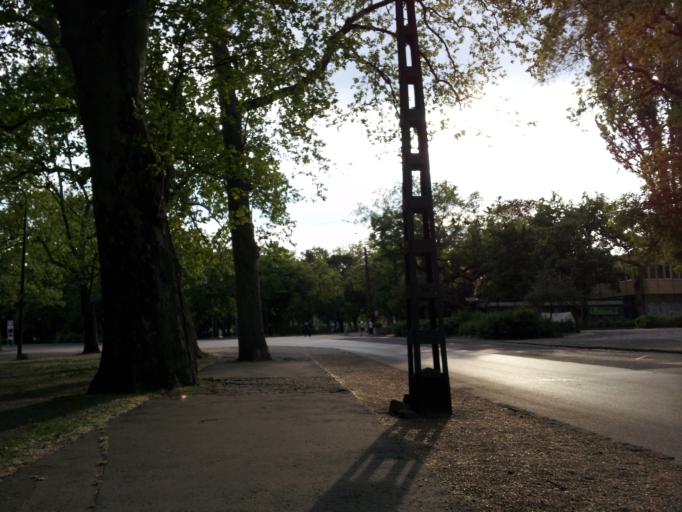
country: HU
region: Budapest
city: Budapest XIII. keruelet
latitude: 47.5131
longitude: 19.0861
